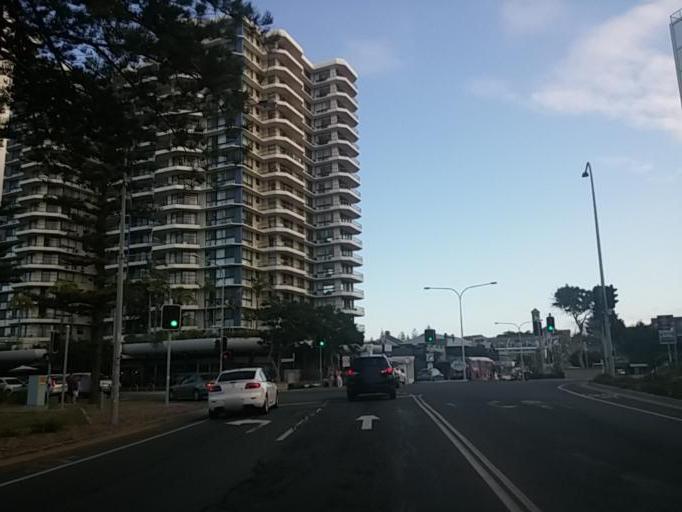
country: AU
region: New South Wales
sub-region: Tweed
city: Tweed Heads West
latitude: -28.1665
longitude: 153.5356
